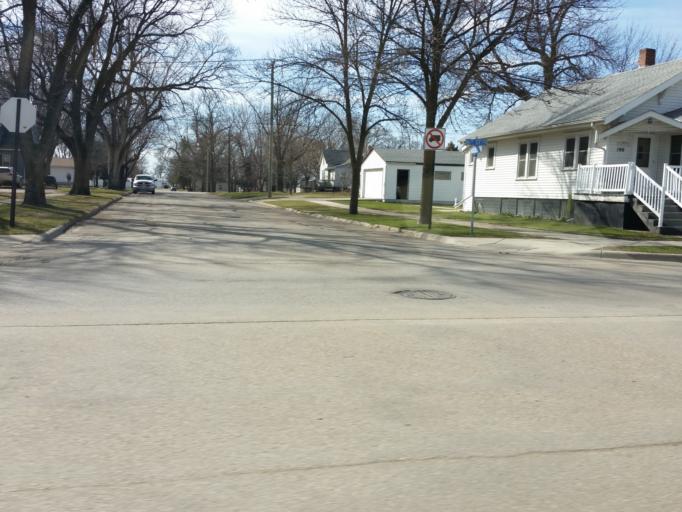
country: US
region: Minnesota
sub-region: Lac qui Parle County
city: Dawson
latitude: 44.9348
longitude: -96.0547
